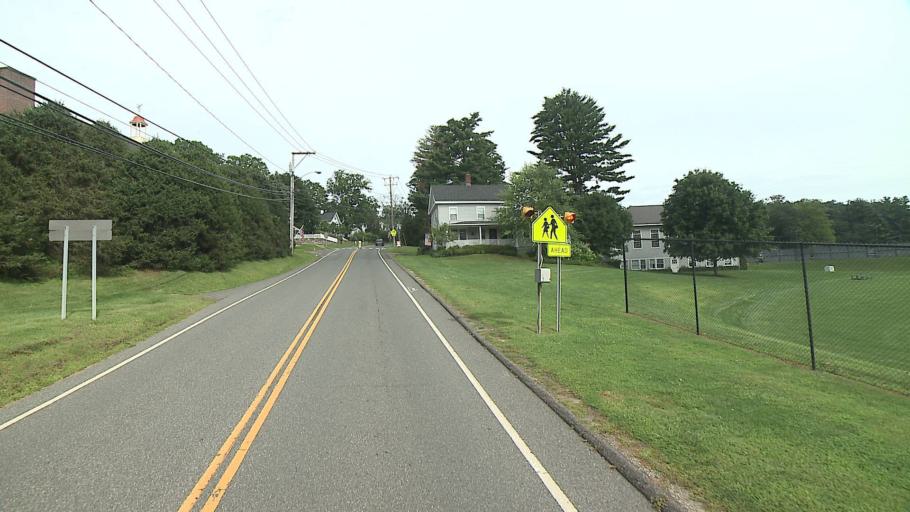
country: US
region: Connecticut
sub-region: Litchfield County
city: New Preston
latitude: 41.6286
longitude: -73.3095
